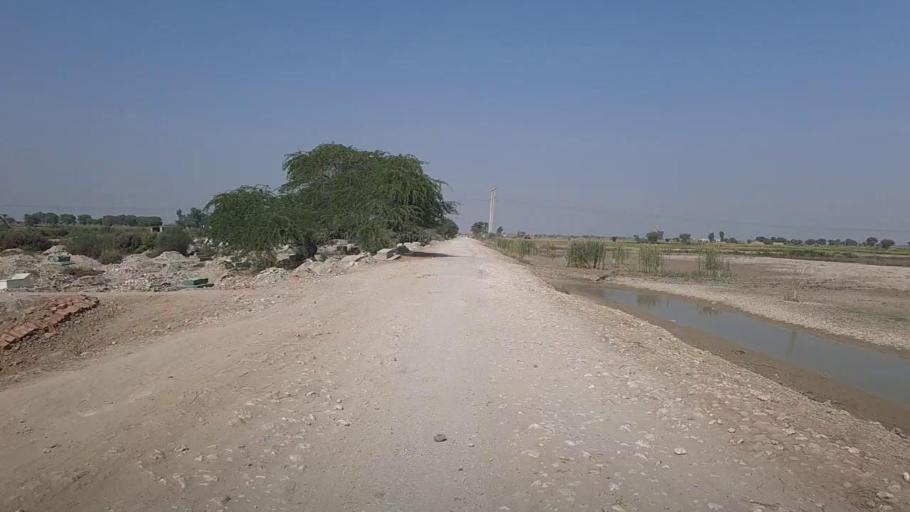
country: PK
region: Sindh
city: Kandhkot
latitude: 28.3905
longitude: 69.3268
